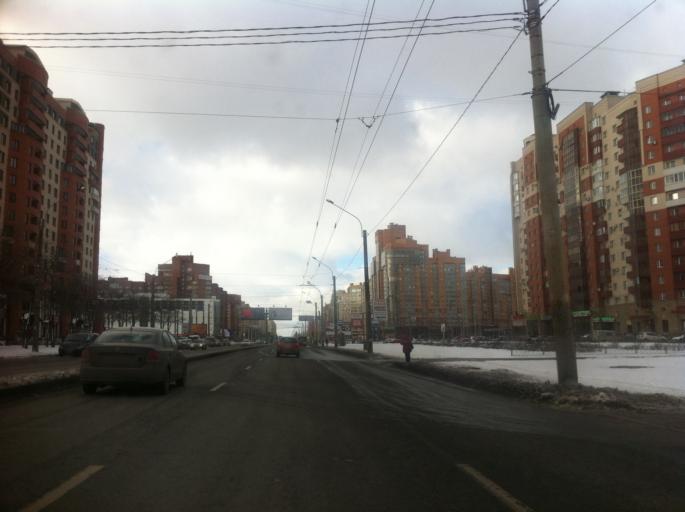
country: RU
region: St.-Petersburg
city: Uritsk
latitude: 59.8553
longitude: 30.2064
